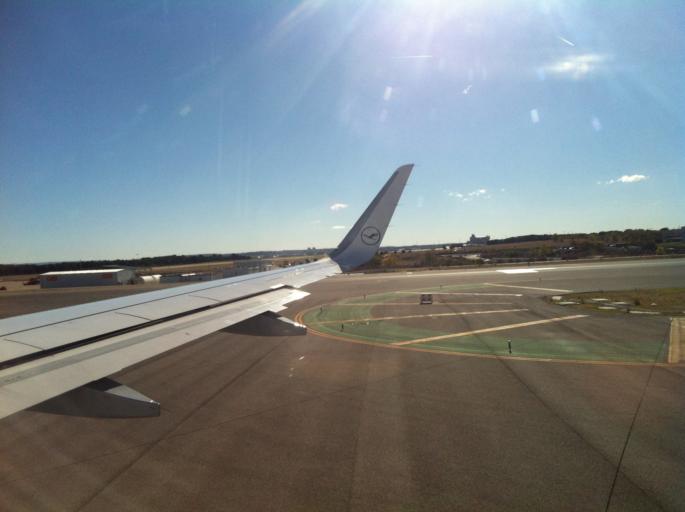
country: ES
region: Madrid
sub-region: Provincia de Madrid
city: Barajas de Madrid
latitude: 40.4886
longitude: -3.5658
